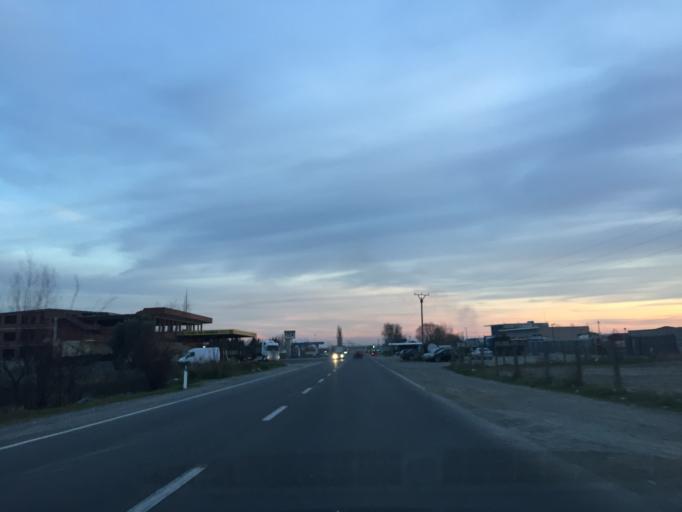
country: AL
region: Lezhe
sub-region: Rrethi i Lezhes
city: Shenkoll
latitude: 41.6700
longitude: 19.6737
